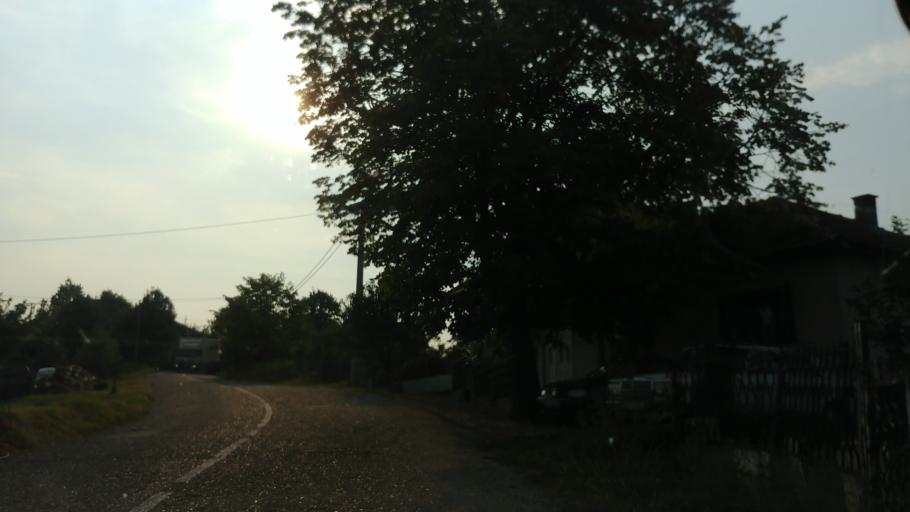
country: BA
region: Republika Srpska
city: Lopare
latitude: 44.7118
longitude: 18.8833
